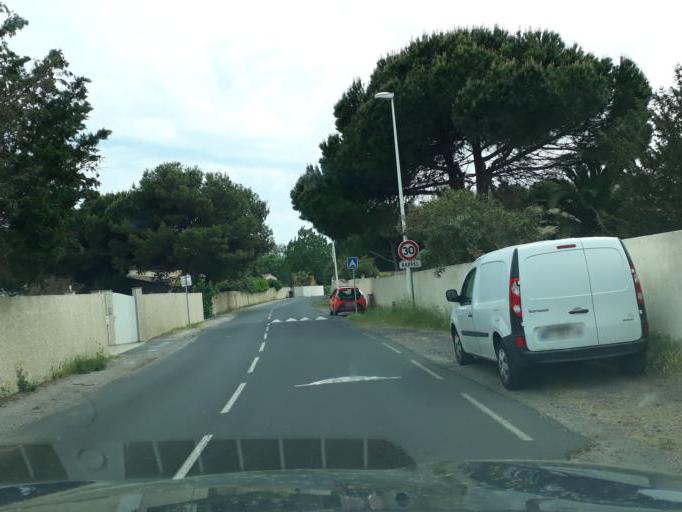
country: FR
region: Languedoc-Roussillon
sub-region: Departement de l'Herault
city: Agde
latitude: 43.2864
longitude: 3.4693
